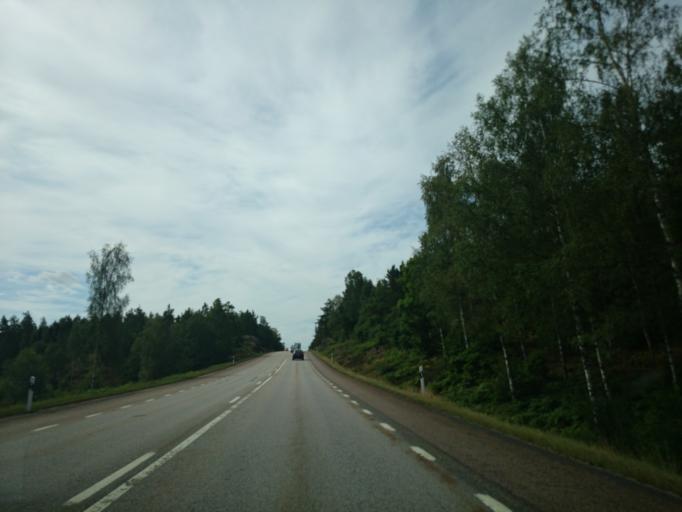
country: SE
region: Kalmar
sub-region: Oskarshamns Kommun
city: Oskarshamn
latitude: 57.4666
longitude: 16.5170
